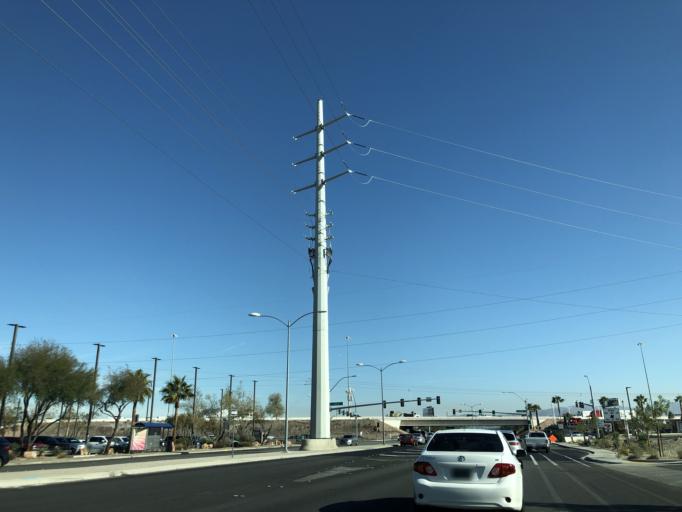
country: US
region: Nevada
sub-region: Clark County
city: Henderson
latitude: 36.0563
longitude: -115.0302
